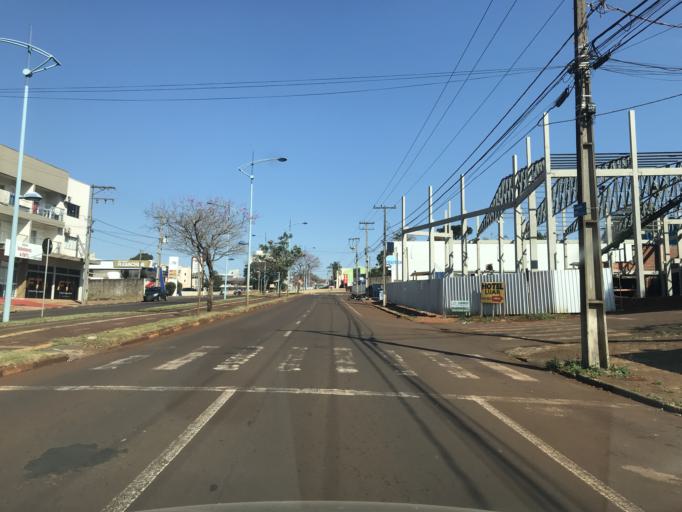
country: BR
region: Parana
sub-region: Toledo
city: Toledo
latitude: -24.7264
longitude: -53.7346
